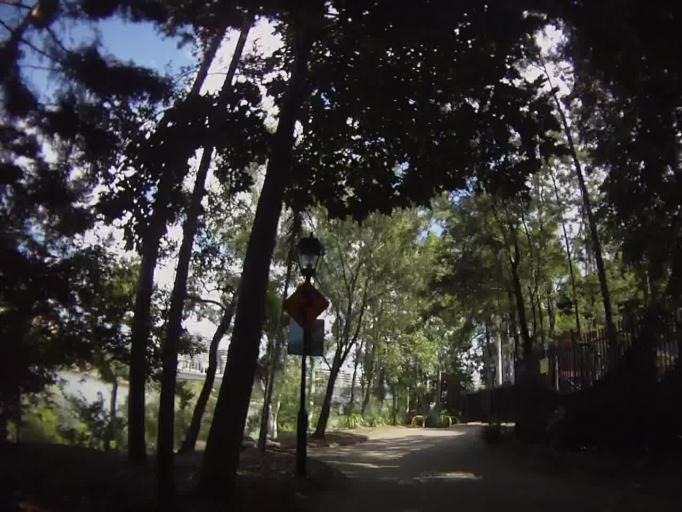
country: AU
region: Queensland
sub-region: Brisbane
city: South Brisbane
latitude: -27.4789
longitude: 153.0306
